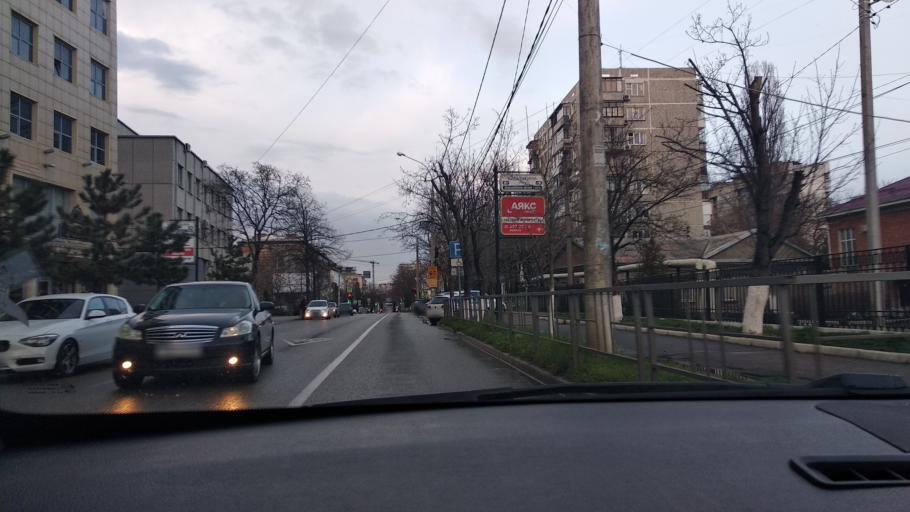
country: RU
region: Krasnodarskiy
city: Krasnodar
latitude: 45.0457
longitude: 38.9753
